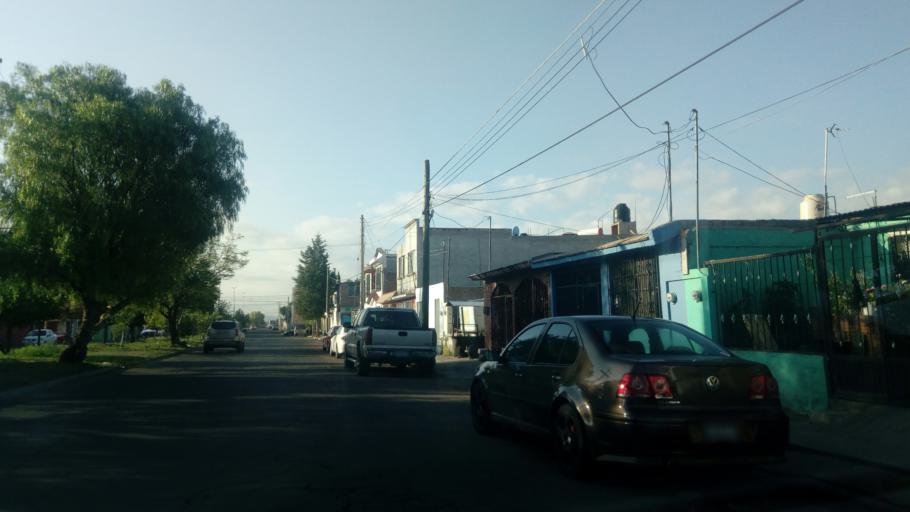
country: MX
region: Durango
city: Victoria de Durango
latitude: 24.0436
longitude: -104.6125
